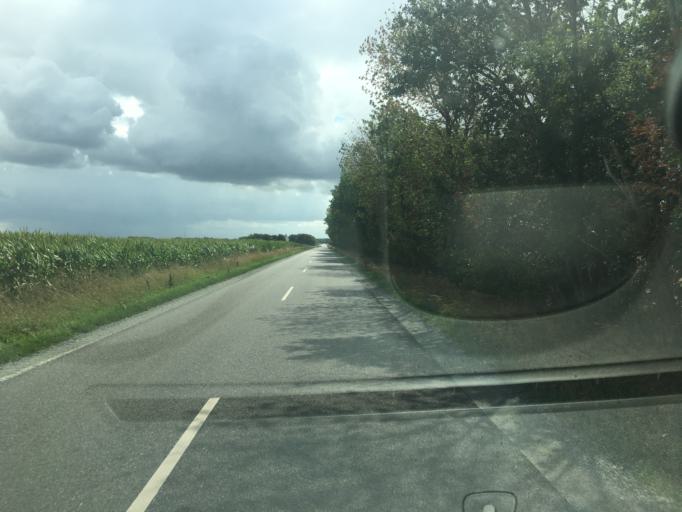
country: DK
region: South Denmark
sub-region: Tonder Kommune
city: Logumkloster
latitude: 55.0479
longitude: 8.9605
